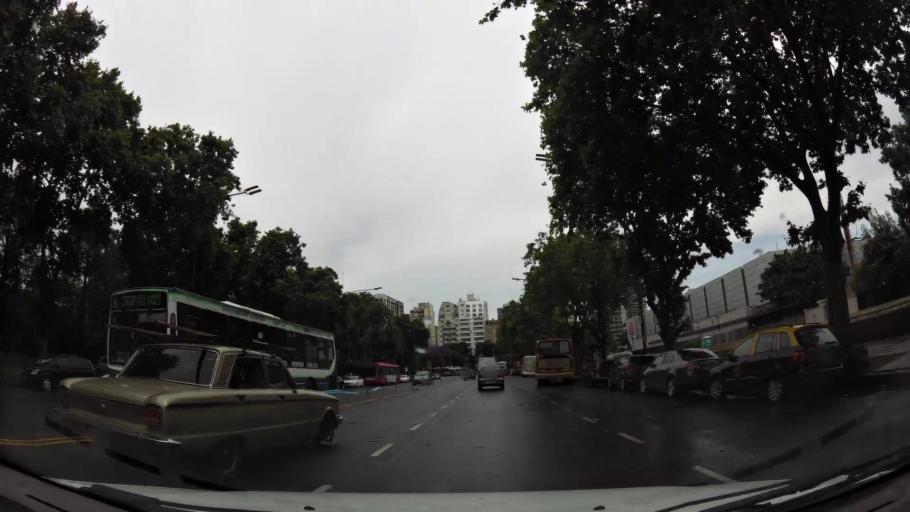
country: AR
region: Buenos Aires F.D.
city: Colegiales
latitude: -34.5797
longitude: -58.4195
